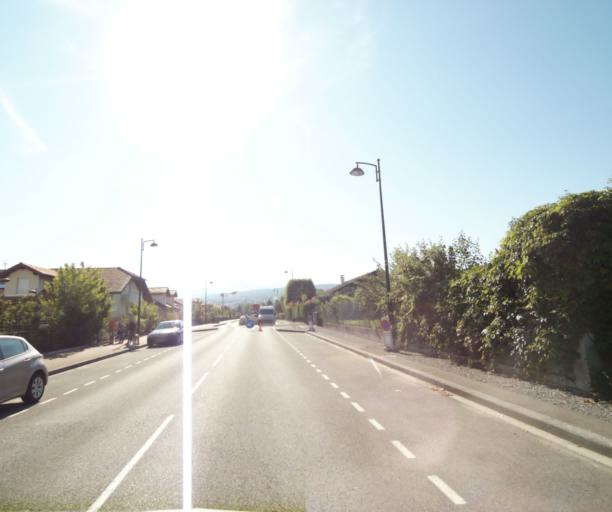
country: FR
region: Rhone-Alpes
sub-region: Departement de la Haute-Savoie
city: Thonon-les-Bains
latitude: 46.3859
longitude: 6.4935
